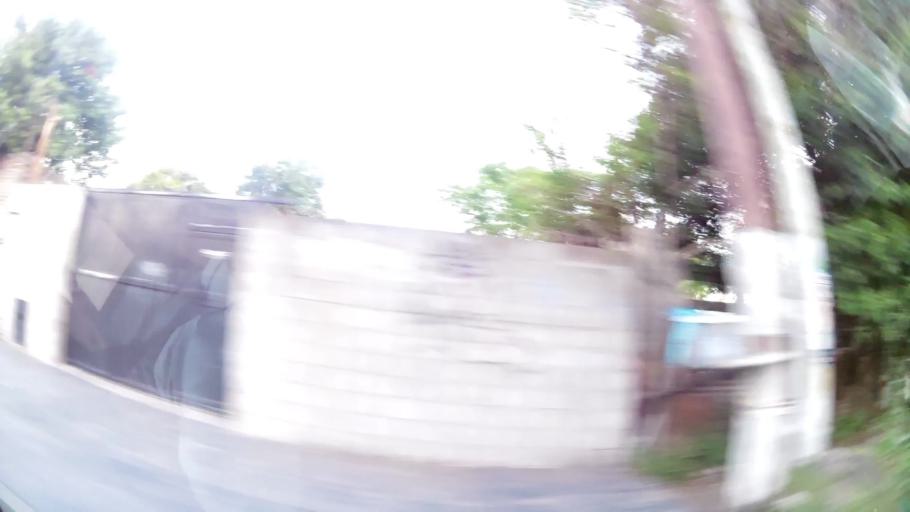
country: AR
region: Buenos Aires
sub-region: Partido de Quilmes
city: Quilmes
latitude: -34.7725
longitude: -58.2029
